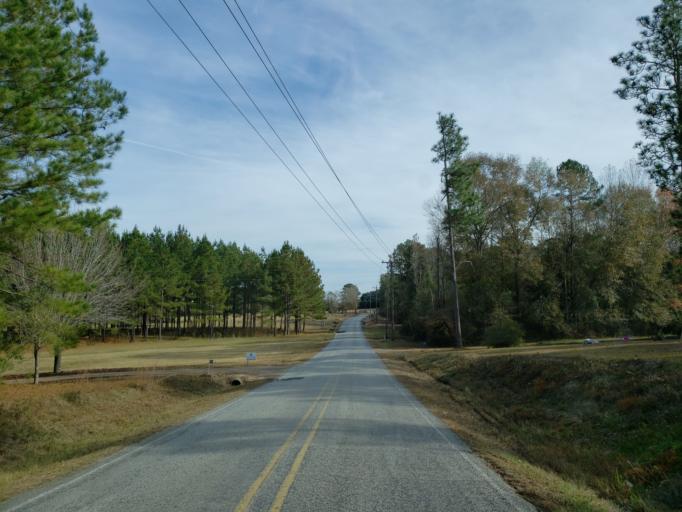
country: US
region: Mississippi
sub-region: Forrest County
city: Rawls Springs
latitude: 31.4126
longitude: -89.4121
